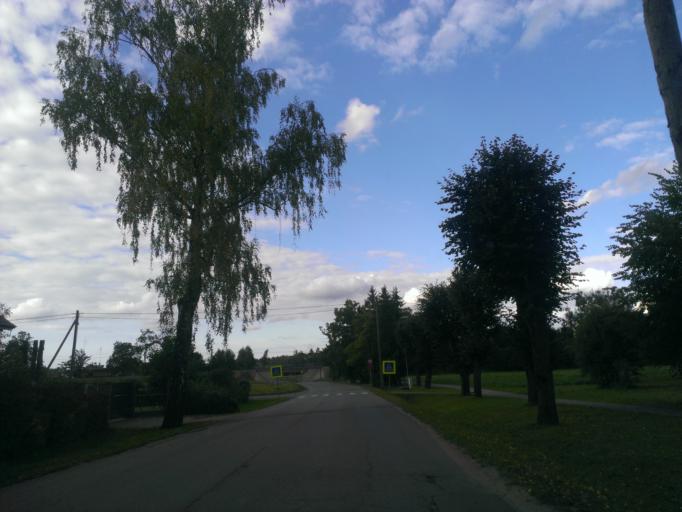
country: LV
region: Sigulda
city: Sigulda
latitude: 57.1540
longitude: 24.8754
